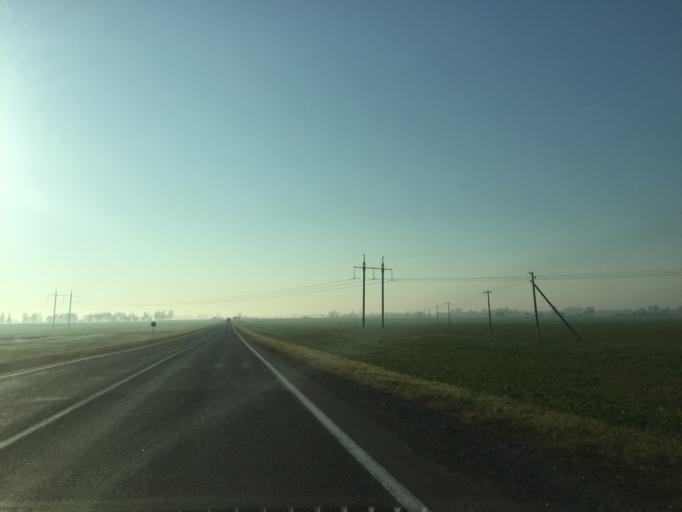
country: BY
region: Gomel
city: Buda-Kashalyova
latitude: 52.8272
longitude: 30.7156
